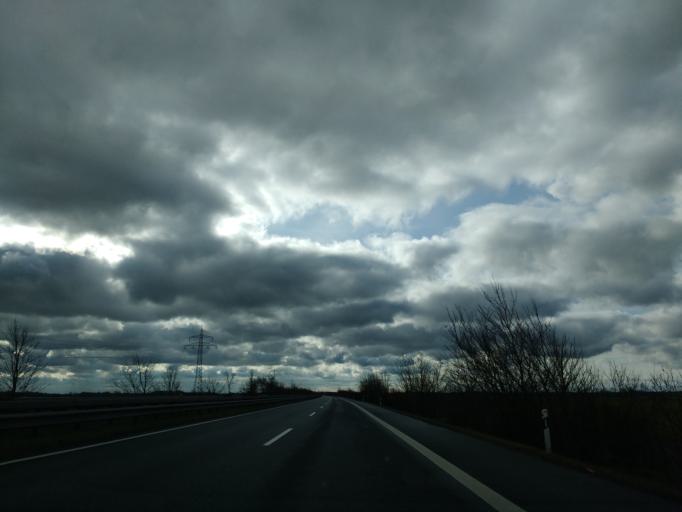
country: DE
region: Lower Saxony
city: Cuxhaven
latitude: 53.8060
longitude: 8.7068
